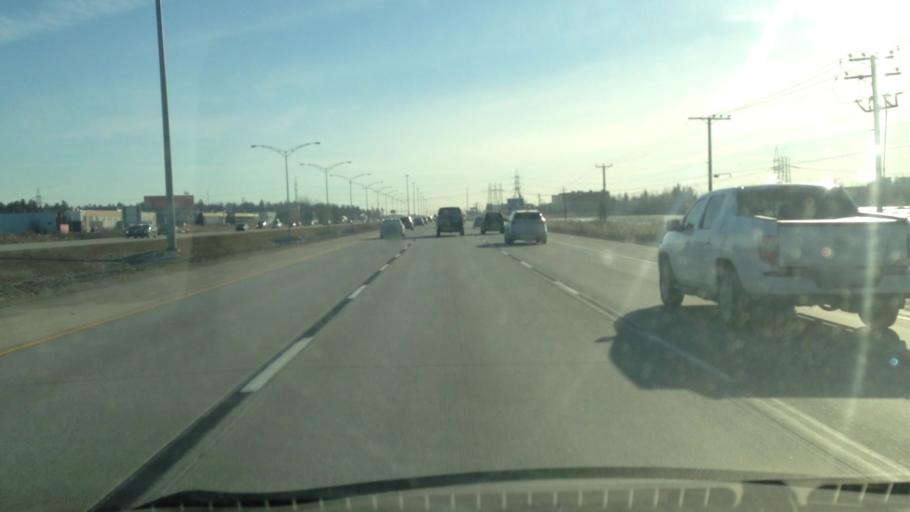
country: CA
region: Quebec
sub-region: Laurentides
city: Blainville
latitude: 45.6885
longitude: -73.9314
